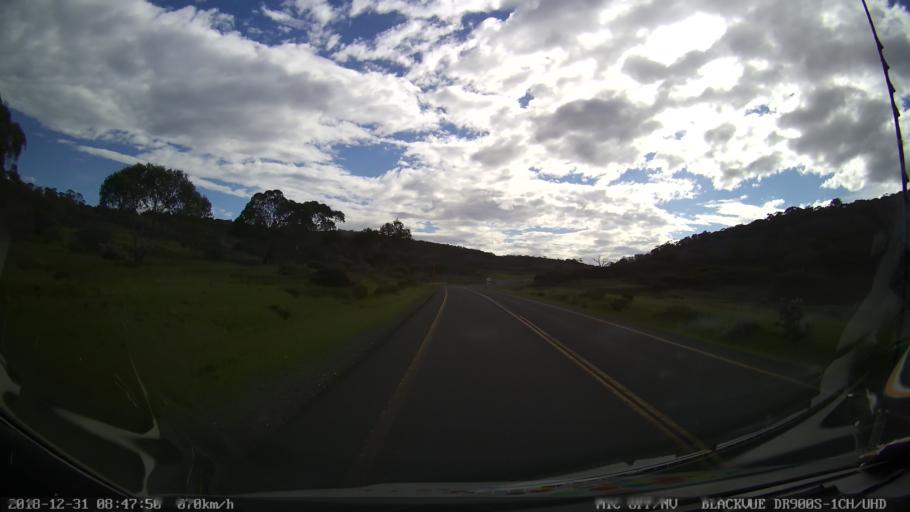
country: AU
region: New South Wales
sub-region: Snowy River
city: Jindabyne
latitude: -36.3601
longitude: 148.4889
